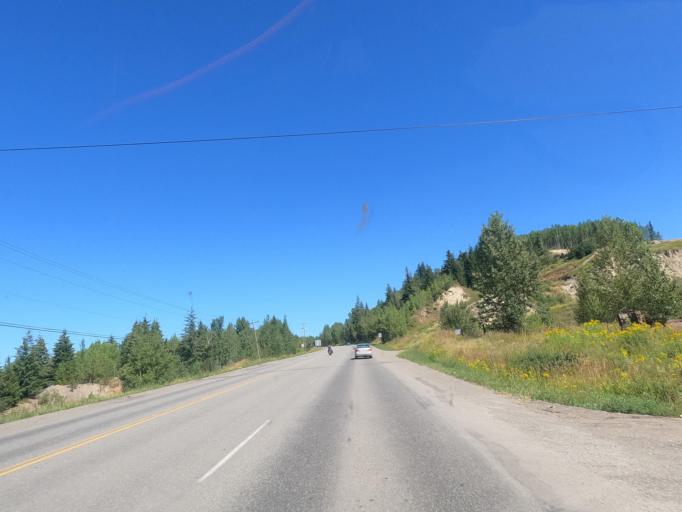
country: CA
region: British Columbia
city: Quesnel
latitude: 53.0190
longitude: -122.4949
